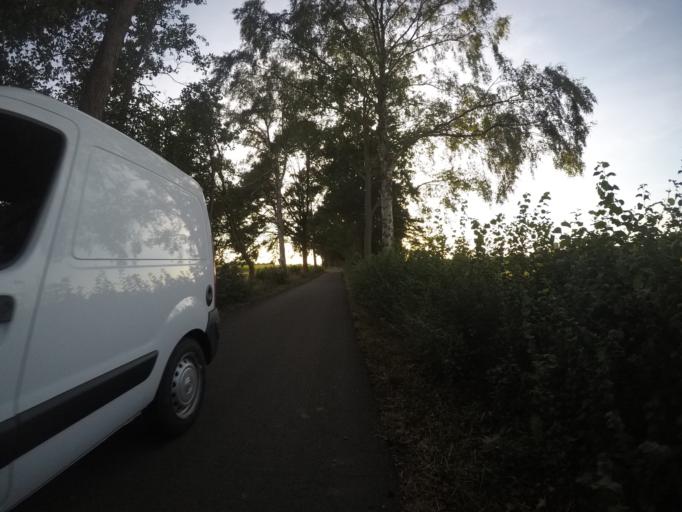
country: DE
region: North Rhine-Westphalia
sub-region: Regierungsbezirk Munster
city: Isselburg
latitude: 51.8489
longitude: 6.4983
